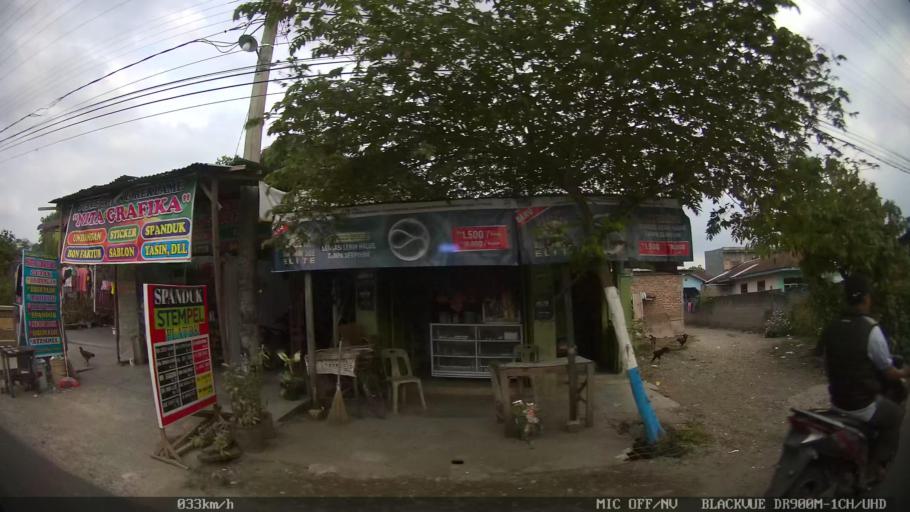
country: ID
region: North Sumatra
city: Sunggal
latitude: 3.5600
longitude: 98.5607
